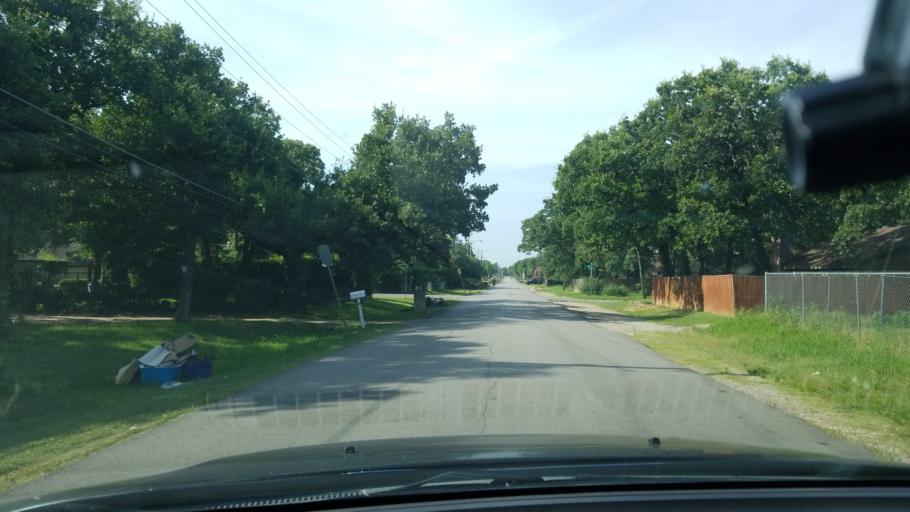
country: US
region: Texas
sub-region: Dallas County
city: Balch Springs
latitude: 32.7292
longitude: -96.6392
